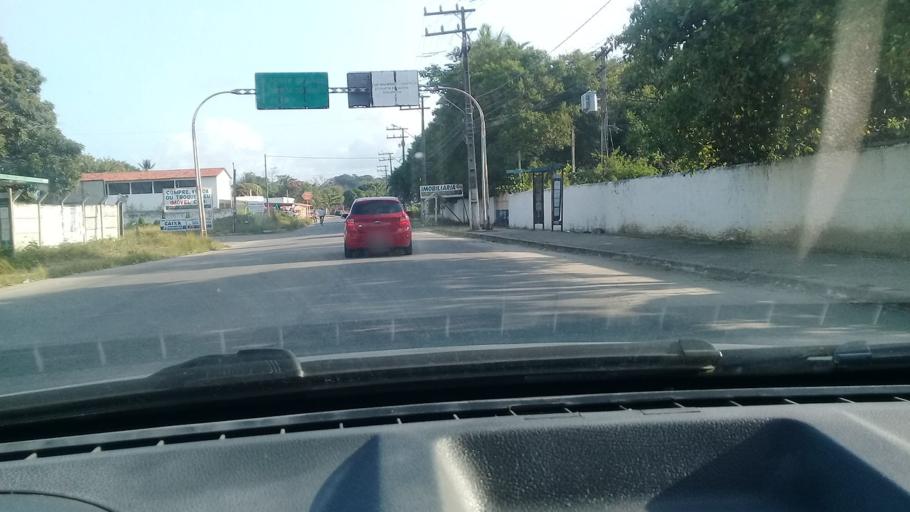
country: BR
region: Pernambuco
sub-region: Itamaraca
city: Itamaraca
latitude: -7.7692
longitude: -34.8359
